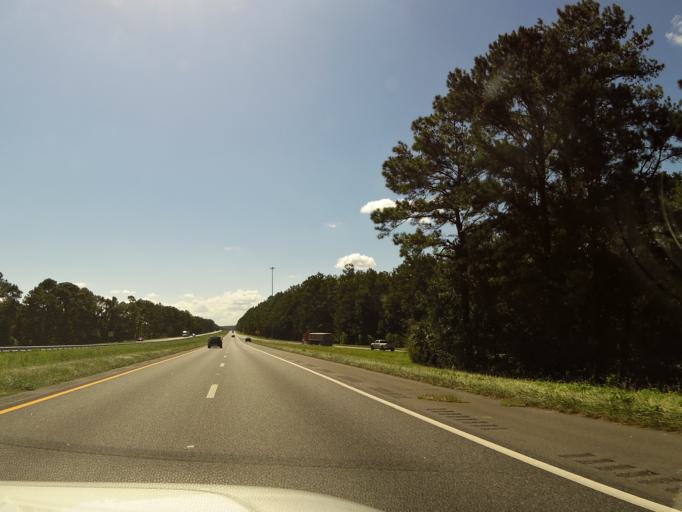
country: US
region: Florida
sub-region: Jefferson County
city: Monticello
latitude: 30.4875
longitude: -84.0271
